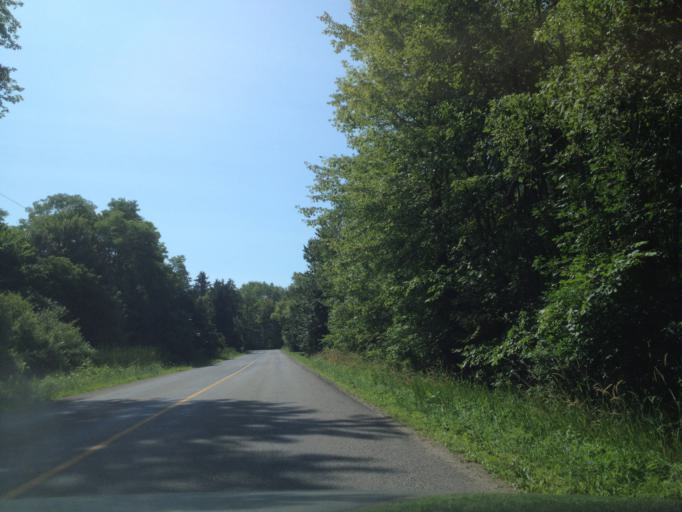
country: CA
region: Ontario
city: Norfolk County
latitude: 42.8147
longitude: -80.3765
